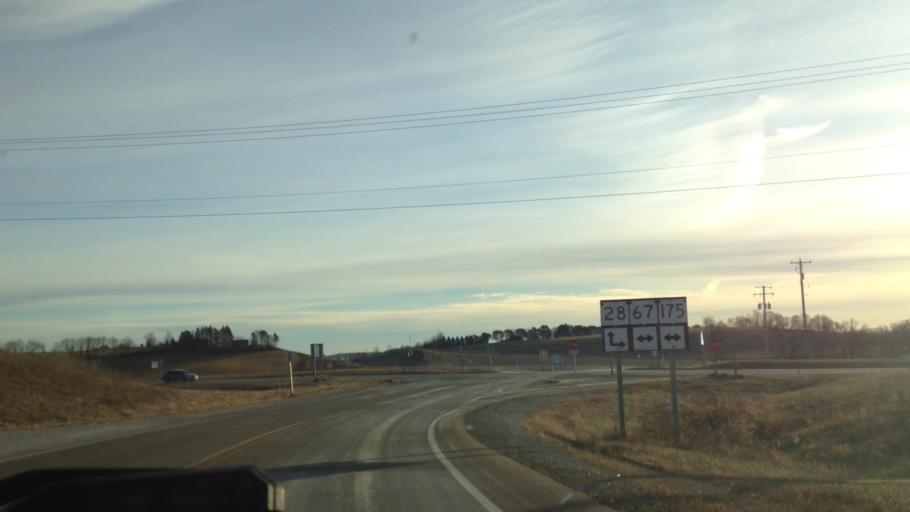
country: US
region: Wisconsin
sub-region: Dodge County
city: Theresa
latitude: 43.5364
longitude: -88.4482
